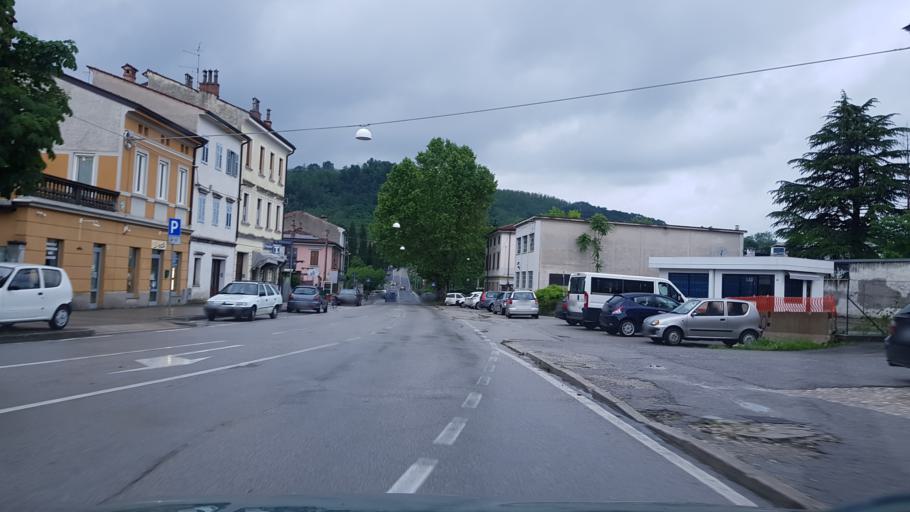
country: IT
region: Friuli Venezia Giulia
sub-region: Provincia di Gorizia
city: Gorizia
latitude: 45.9549
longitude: 13.6159
